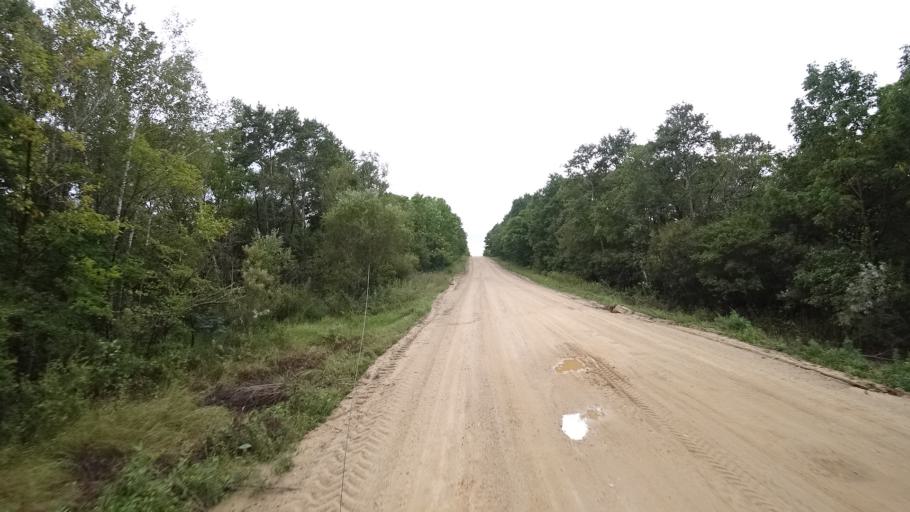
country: RU
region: Primorskiy
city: Monastyrishche
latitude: 44.1115
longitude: 132.6211
